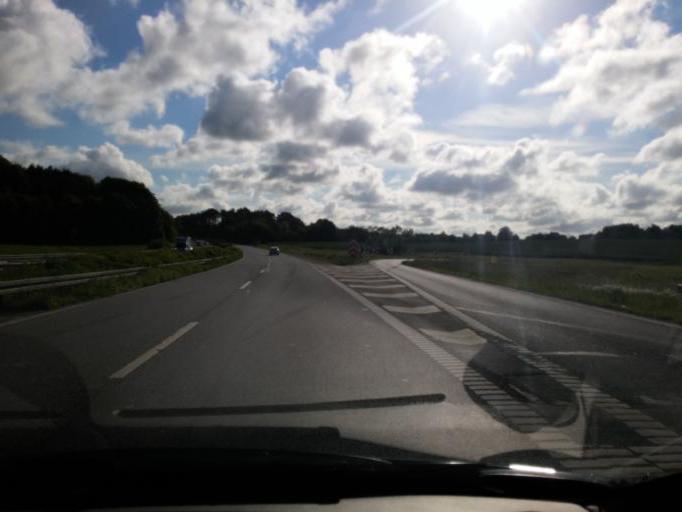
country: DK
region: Zealand
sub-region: Slagelse Kommune
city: Slagelse
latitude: 55.3893
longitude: 11.3620
